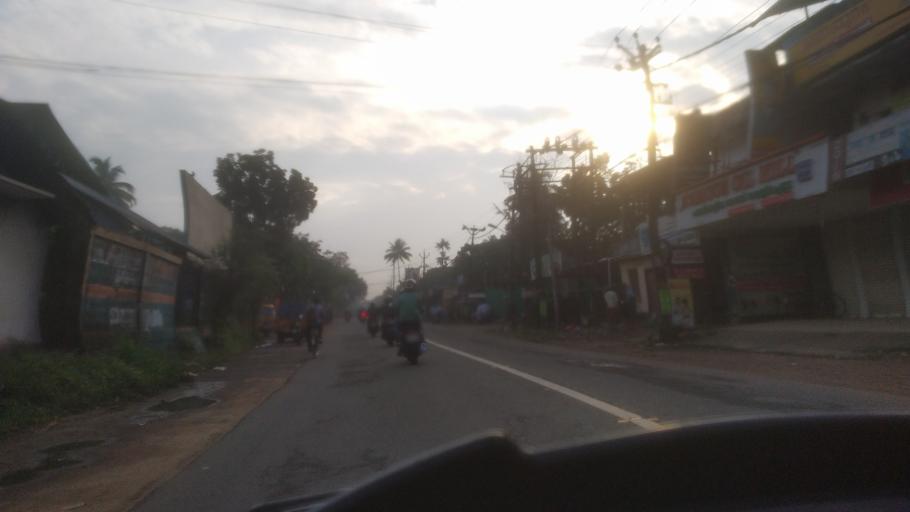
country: IN
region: Kerala
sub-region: Ernakulam
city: Perumpavur
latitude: 10.1159
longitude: 76.4477
